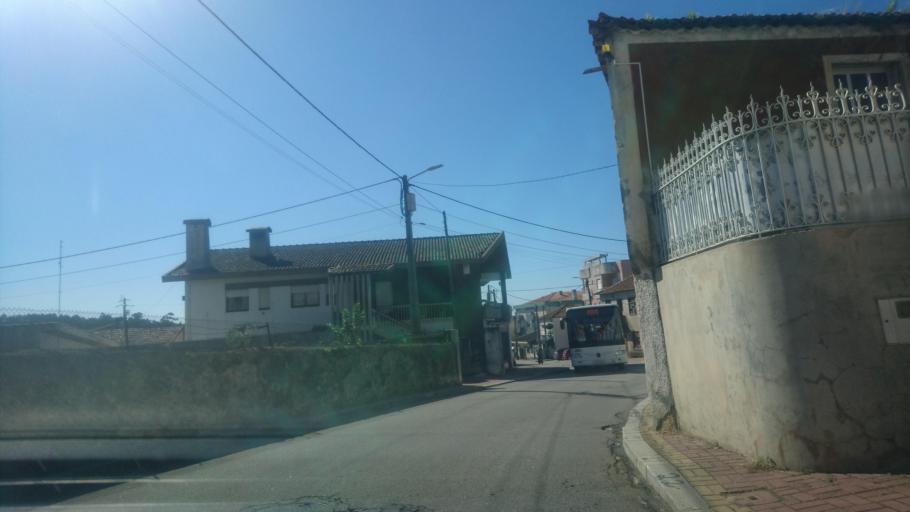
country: PT
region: Aveiro
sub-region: Santa Maria da Feira
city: Lamas
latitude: 40.9815
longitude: -8.5704
